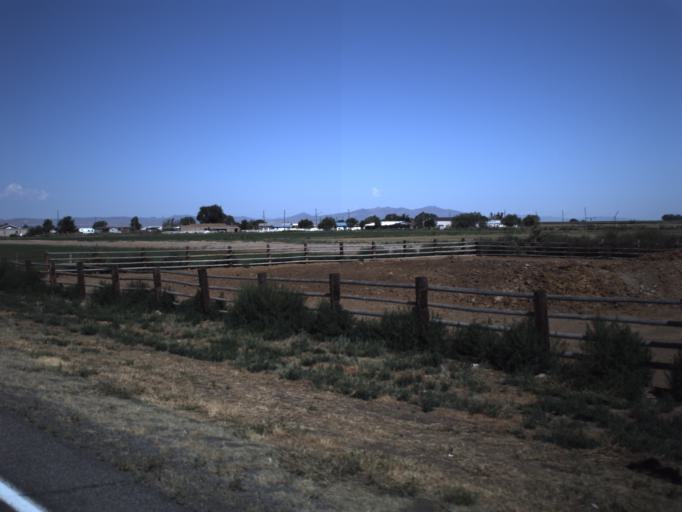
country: US
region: Utah
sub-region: Millard County
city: Delta
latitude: 39.3308
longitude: -112.6723
